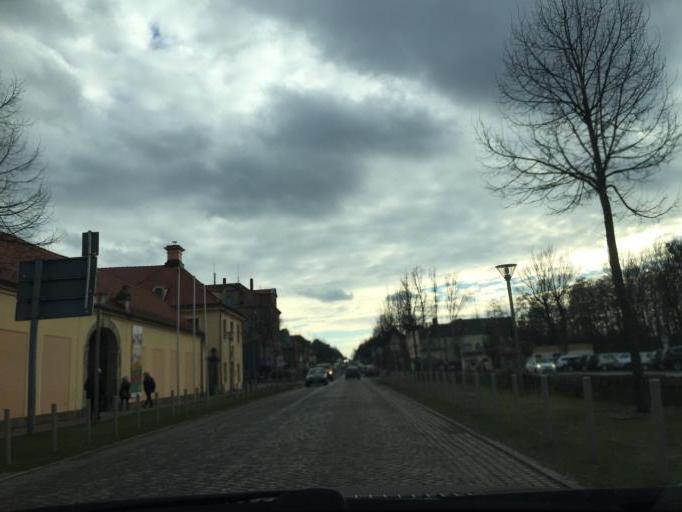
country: DE
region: Saxony
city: Moritzburg
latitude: 51.1649
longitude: 13.6797
